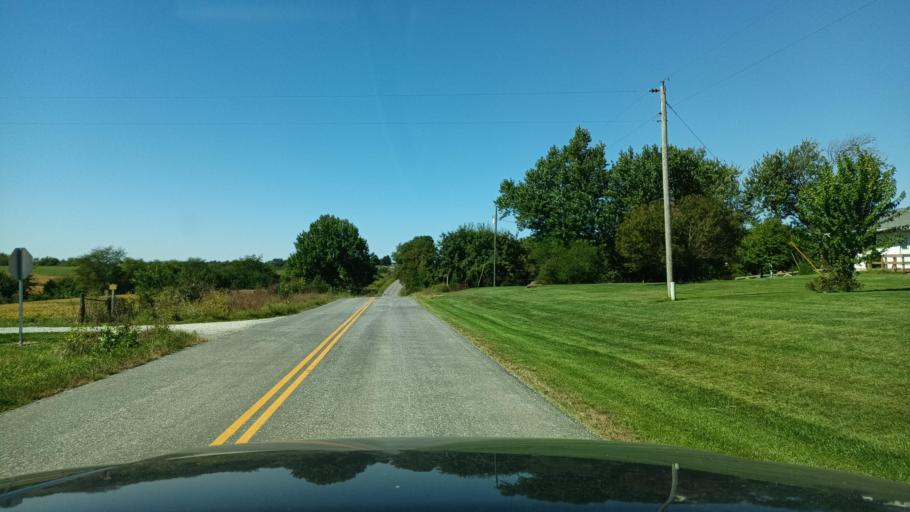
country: US
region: Missouri
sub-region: Adair County
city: Kirksville
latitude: 40.3306
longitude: -92.5022
